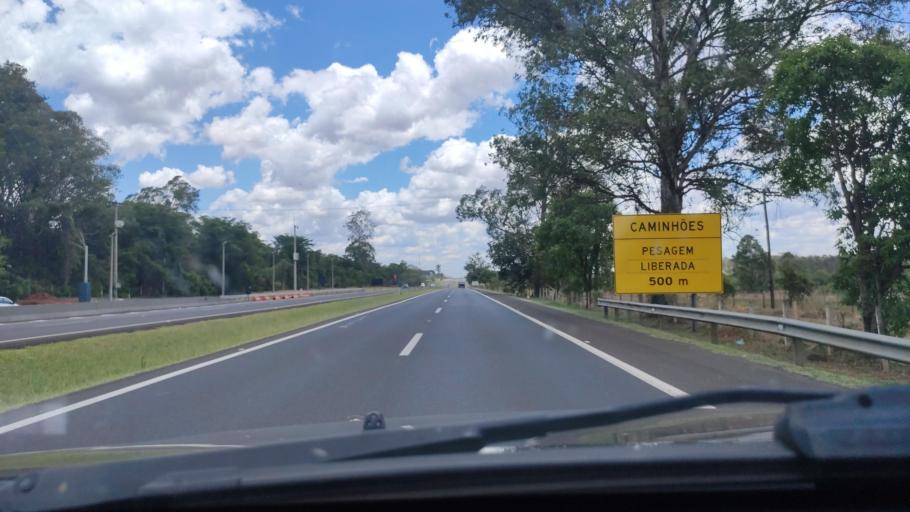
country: BR
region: Sao Paulo
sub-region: Bauru
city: Bauru
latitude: -22.3235
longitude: -48.9582
